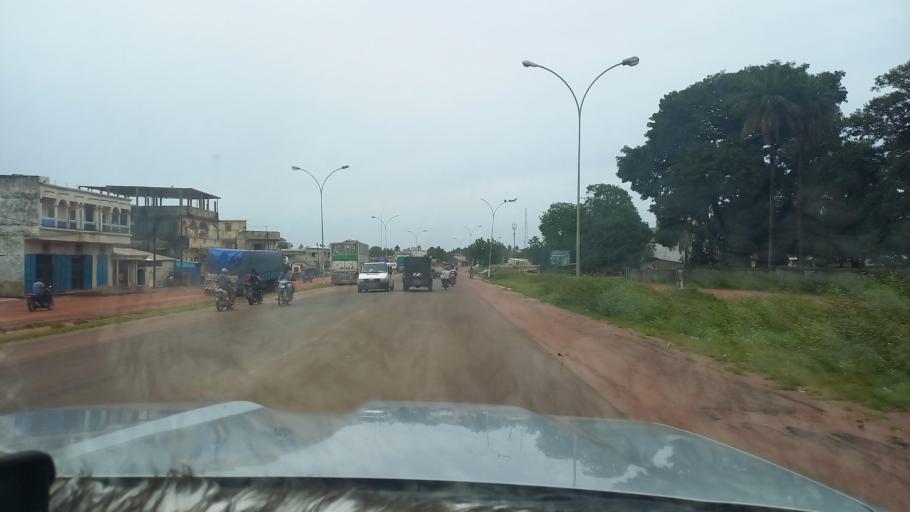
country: SN
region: Ziguinchor
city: Ziguinchor
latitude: 12.5704
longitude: -16.2709
